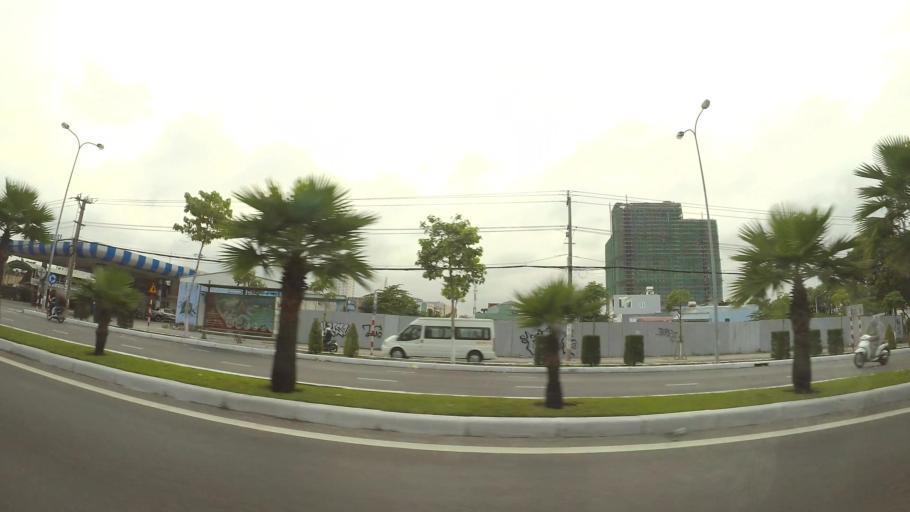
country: VN
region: Da Nang
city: Son Tra
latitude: 16.0545
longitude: 108.2364
